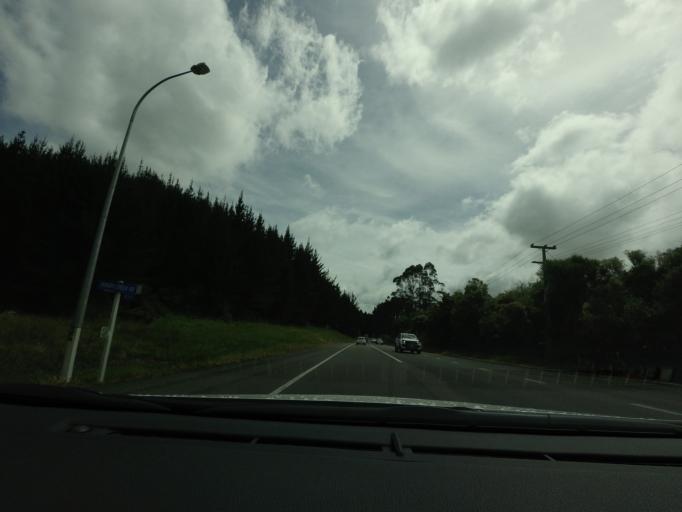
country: NZ
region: Auckland
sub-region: Auckland
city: Warkworth
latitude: -36.5106
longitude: 174.6712
